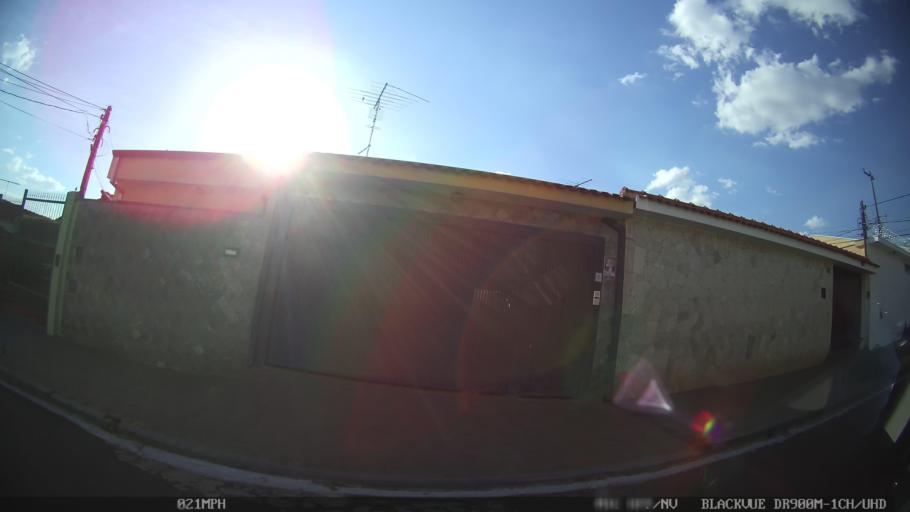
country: BR
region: Sao Paulo
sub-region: Ribeirao Preto
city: Ribeirao Preto
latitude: -21.1897
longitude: -47.7885
